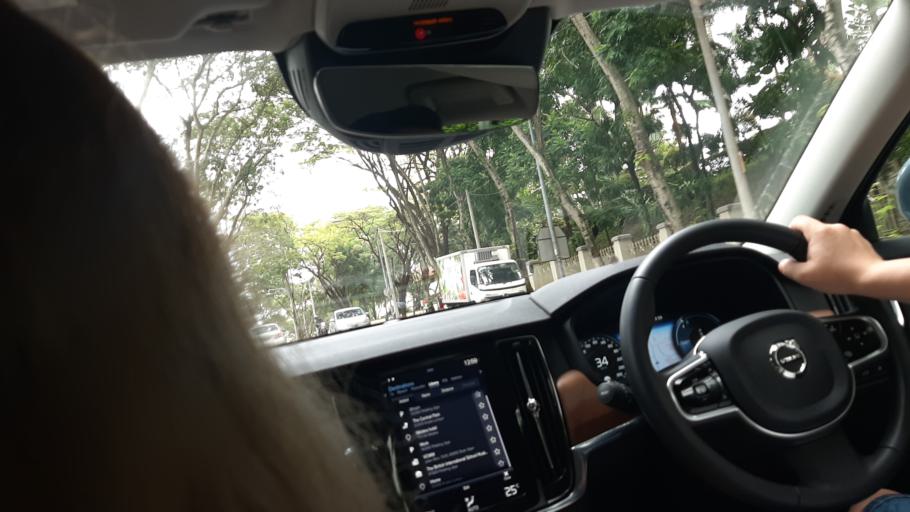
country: MY
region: Kuala Lumpur
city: Kuala Lumpur
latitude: 3.1688
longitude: 101.6526
